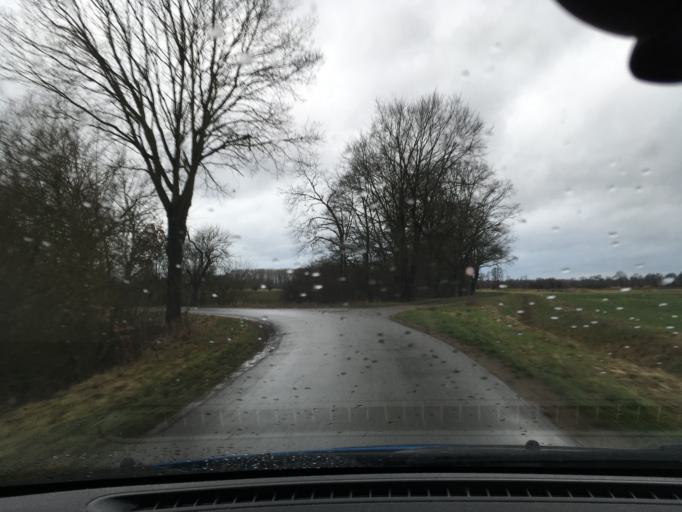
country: DE
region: Lower Saxony
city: Neetze
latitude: 53.3259
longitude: 10.6578
